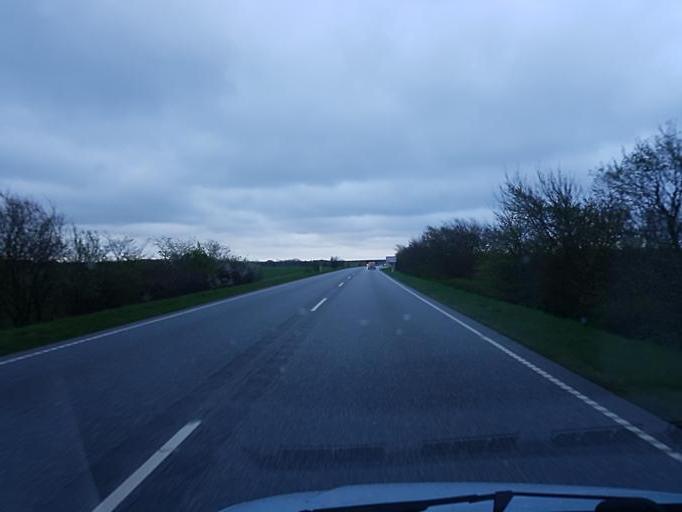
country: DK
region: South Denmark
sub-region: Esbjerg Kommune
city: Bramming
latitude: 55.4103
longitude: 8.7198
